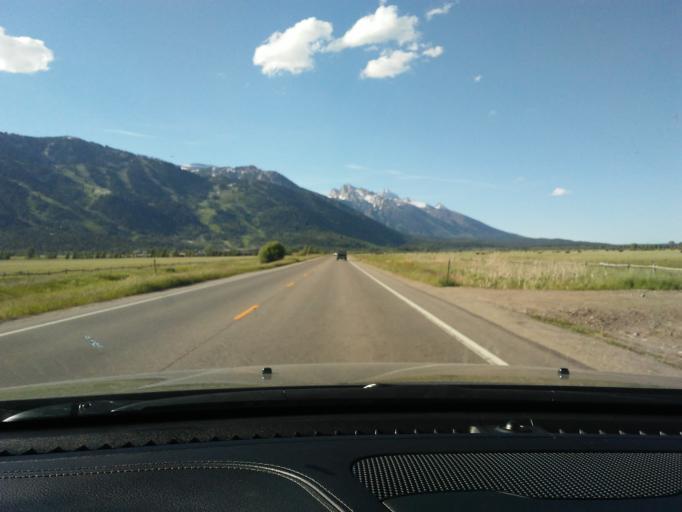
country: US
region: Wyoming
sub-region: Teton County
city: Moose Wilson Road
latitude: 43.5640
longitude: -110.8220
